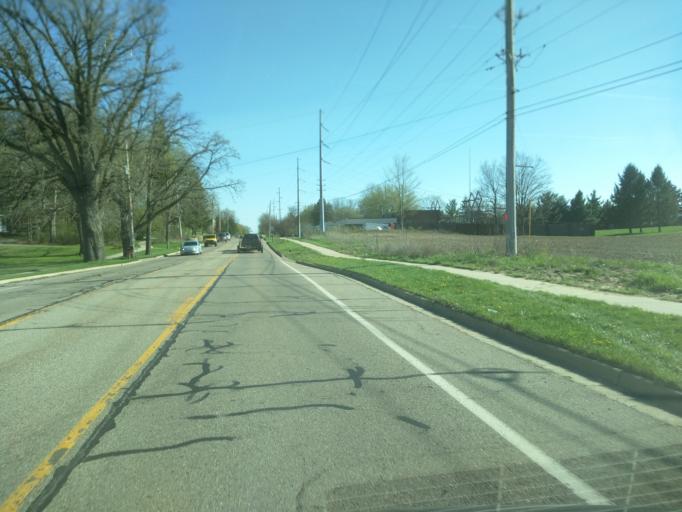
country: US
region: Michigan
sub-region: Eaton County
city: Waverly
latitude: 42.7526
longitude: -84.6422
